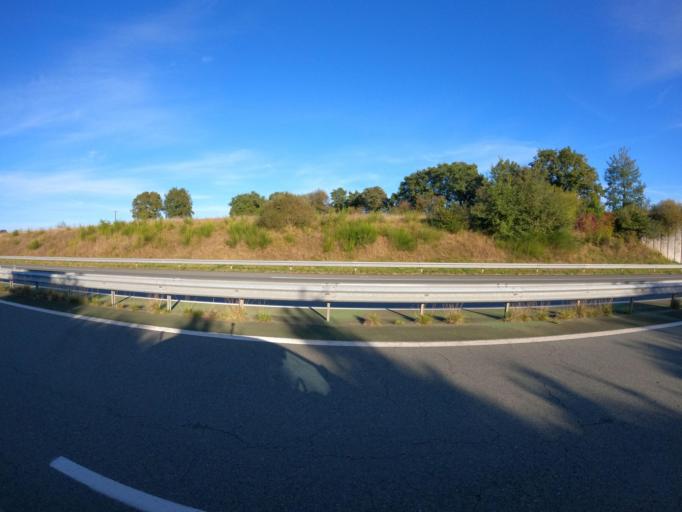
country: FR
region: Pays de la Loire
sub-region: Departement de Maine-et-Loire
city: Trementines
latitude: 47.1248
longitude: -0.8252
